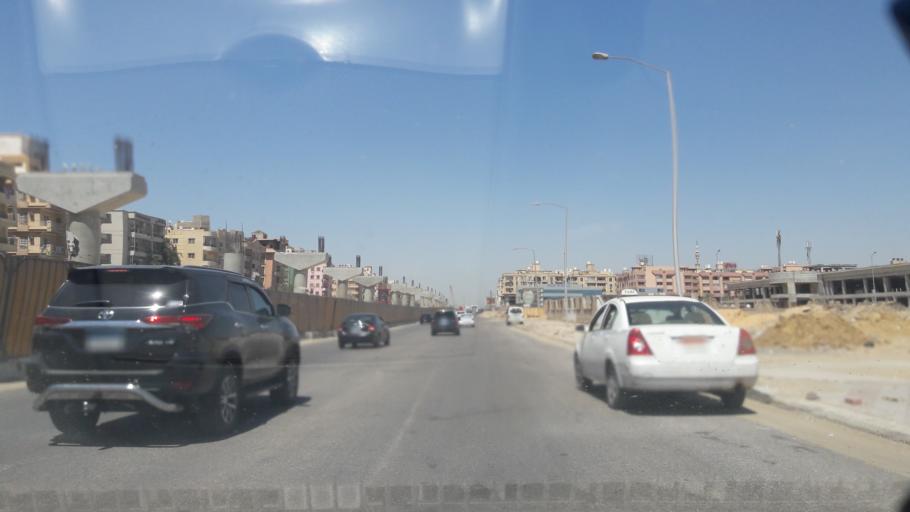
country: EG
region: Al Jizah
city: Madinat Sittah Uktubar
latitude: 29.9702
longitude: 30.9351
